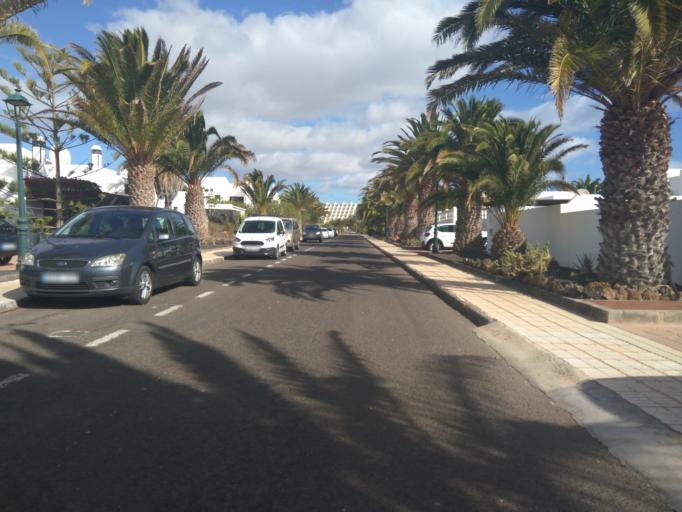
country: ES
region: Canary Islands
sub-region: Provincia de Las Palmas
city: Arrecife
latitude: 29.0062
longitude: -13.4890
